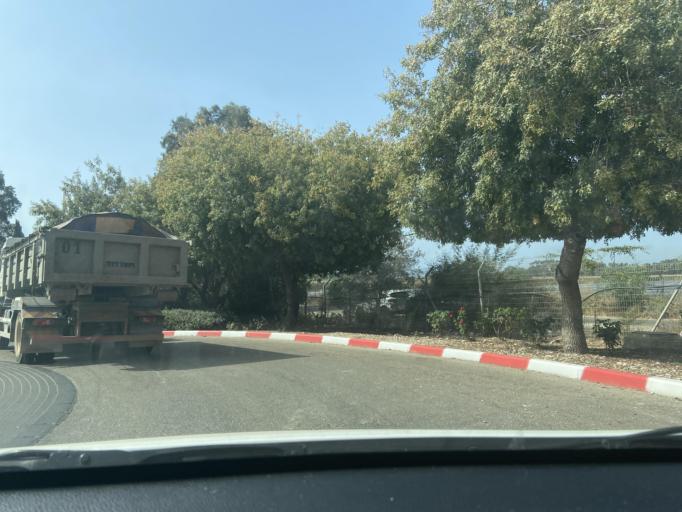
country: IL
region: Northern District
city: Nahariya
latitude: 33.0446
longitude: 35.1088
